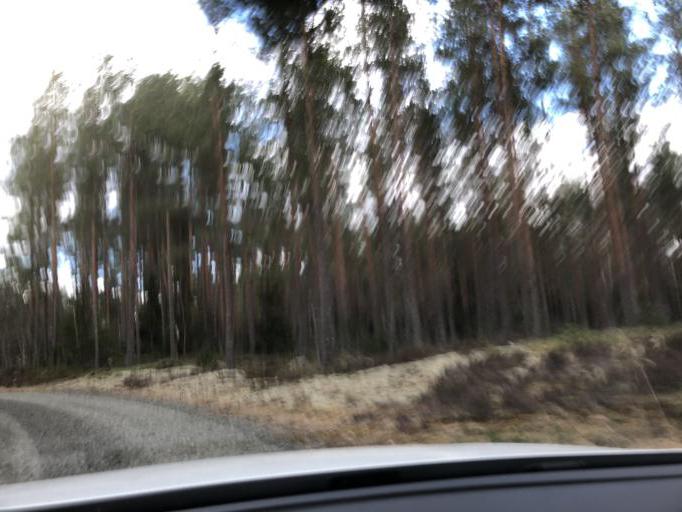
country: SE
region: Uppsala
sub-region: Heby Kommun
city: OEstervala
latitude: 60.3292
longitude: 17.1749
